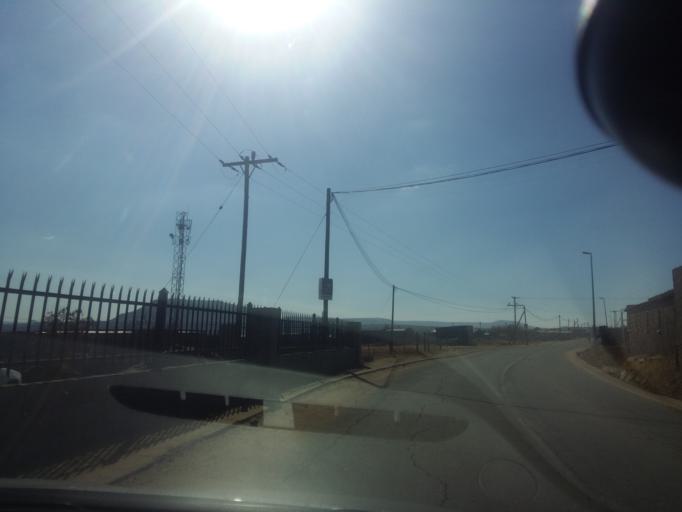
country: LS
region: Maseru
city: Maseru
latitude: -29.3422
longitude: 27.4404
